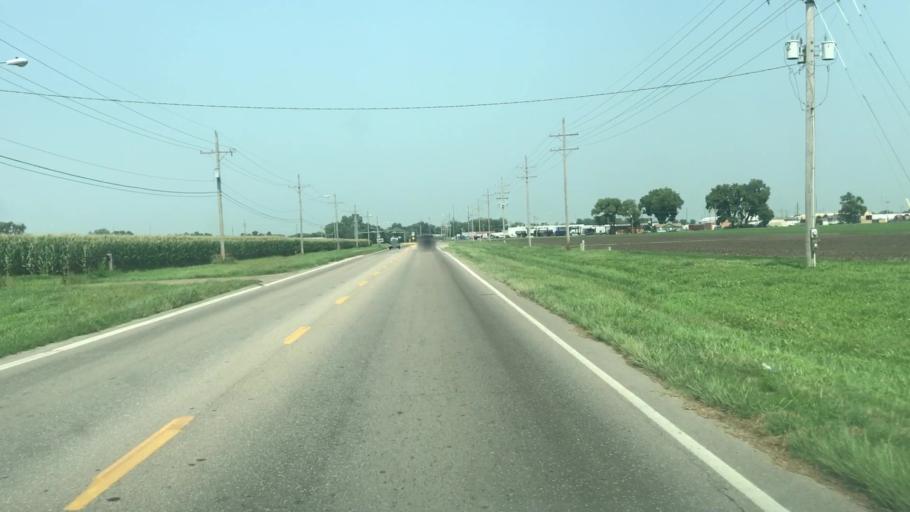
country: US
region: Nebraska
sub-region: Hall County
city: Grand Island
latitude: 40.9274
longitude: -98.3206
